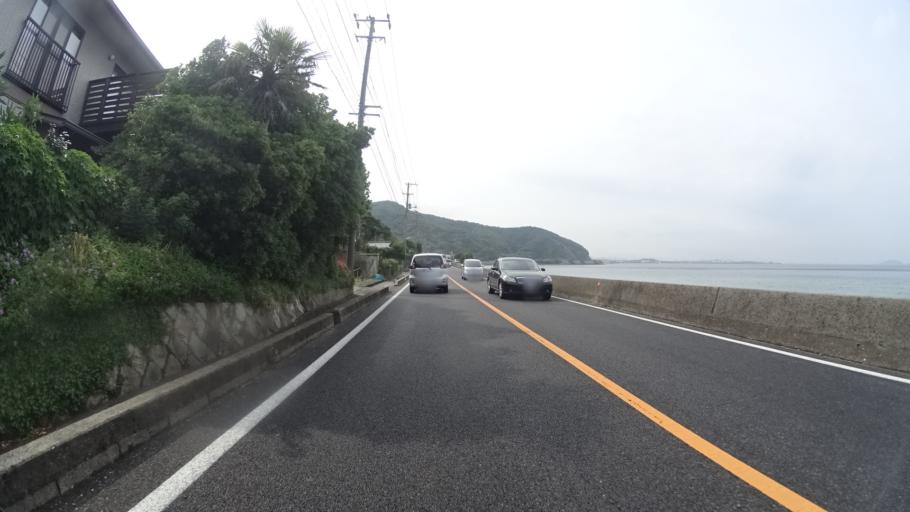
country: JP
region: Yamaguchi
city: Shimonoseki
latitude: 34.0635
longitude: 130.9085
